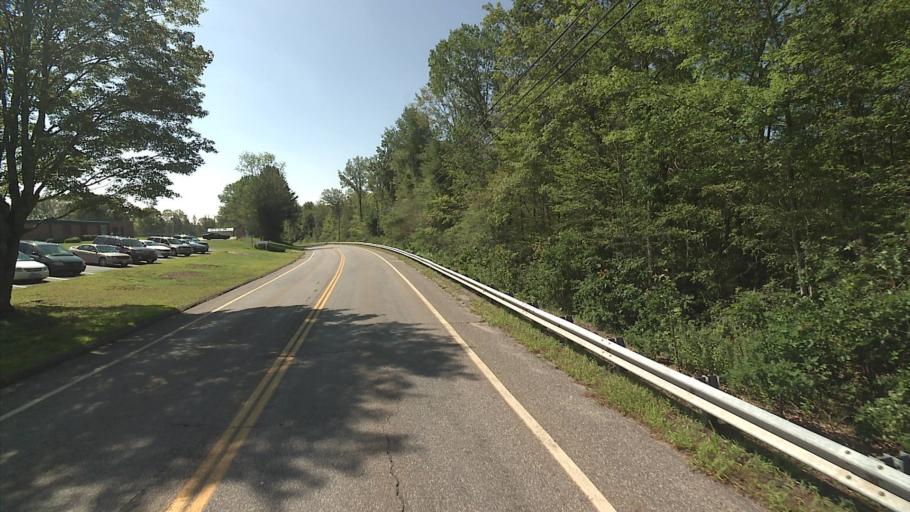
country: US
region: Connecticut
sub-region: Tolland County
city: Storrs
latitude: 41.8931
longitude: -72.1702
